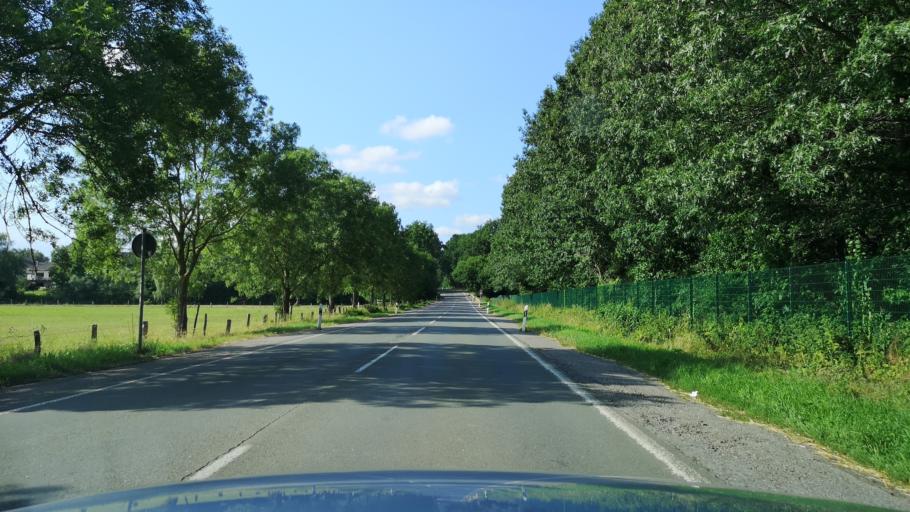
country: DE
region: North Rhine-Westphalia
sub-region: Regierungsbezirk Arnsberg
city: Holzwickede
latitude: 51.4535
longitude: 7.6272
